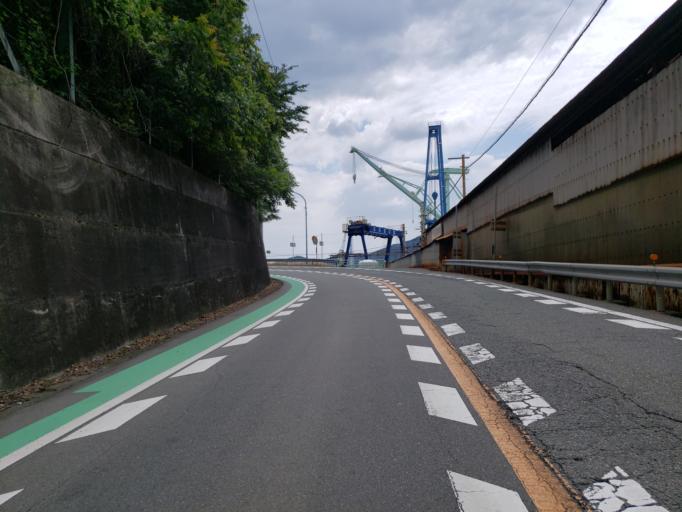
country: JP
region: Hyogo
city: Aioi
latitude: 34.7933
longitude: 134.4686
